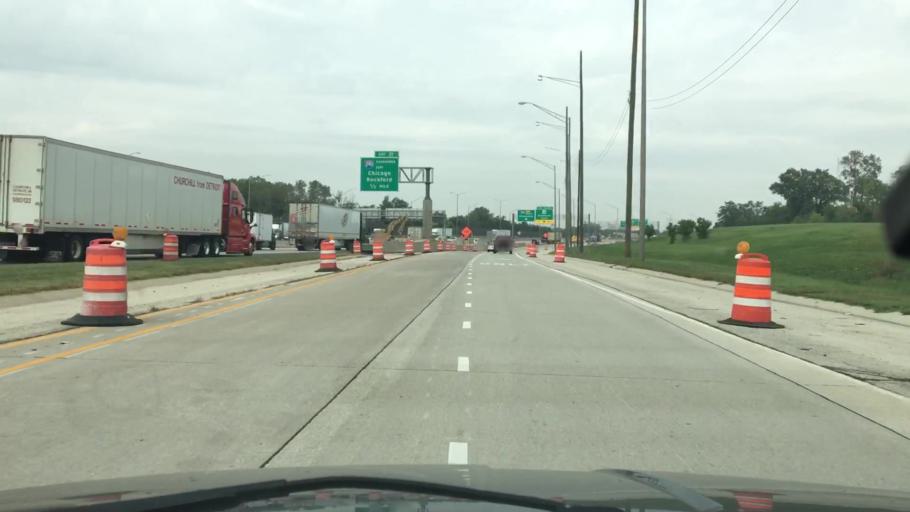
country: US
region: Illinois
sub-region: DuPage County
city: Oak Brook
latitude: 41.8555
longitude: -87.9189
